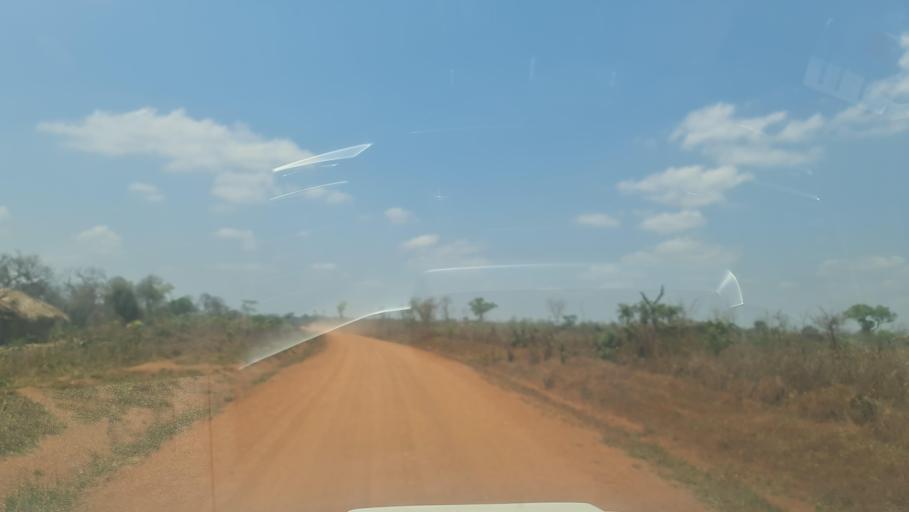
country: MW
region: Southern Region
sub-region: Nsanje District
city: Nsanje
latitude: -17.4222
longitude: 35.8250
